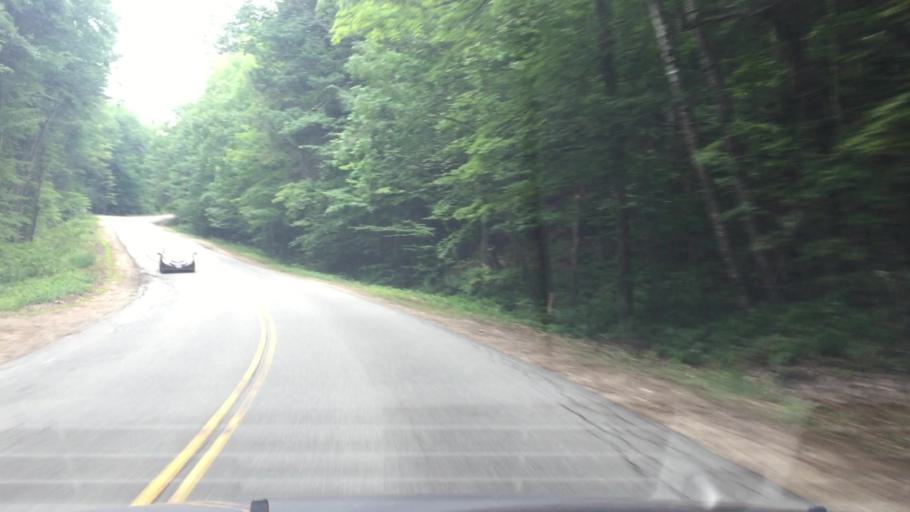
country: US
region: New Hampshire
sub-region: Carroll County
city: North Conway
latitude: 44.0987
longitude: -71.1738
